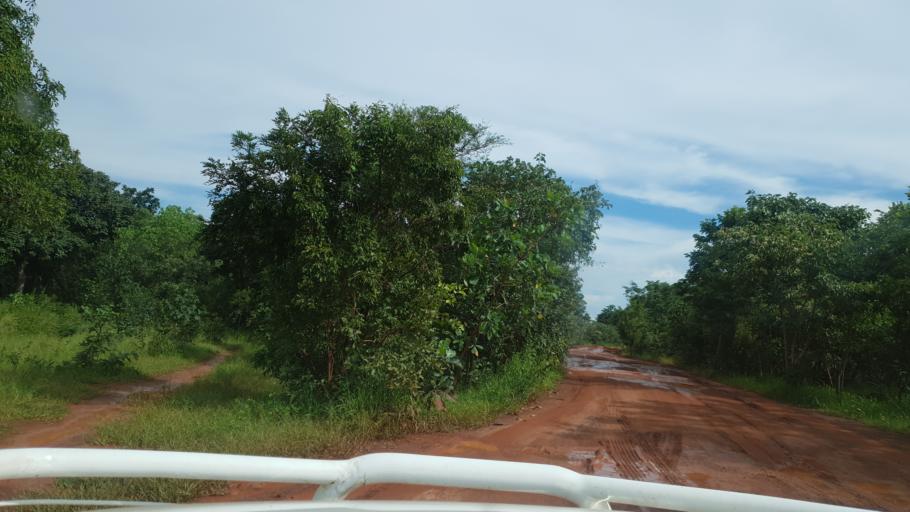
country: ML
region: Sikasso
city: Kolondieba
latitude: 10.7413
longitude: -6.9106
